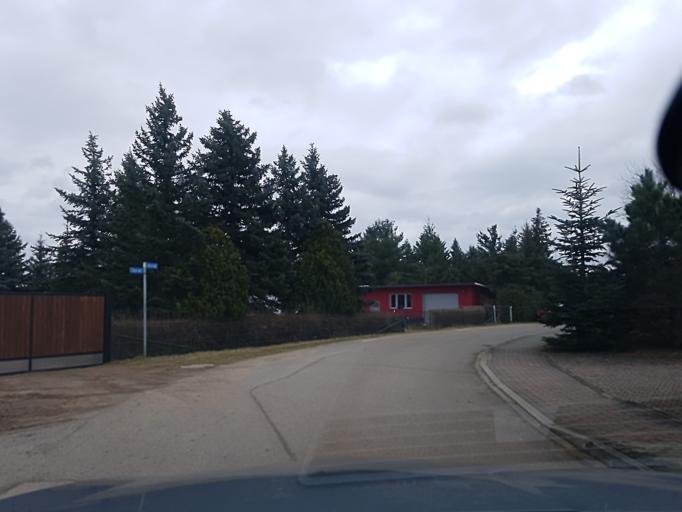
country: DE
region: Brandenburg
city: Bad Liebenwerda
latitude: 51.5453
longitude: 13.3629
